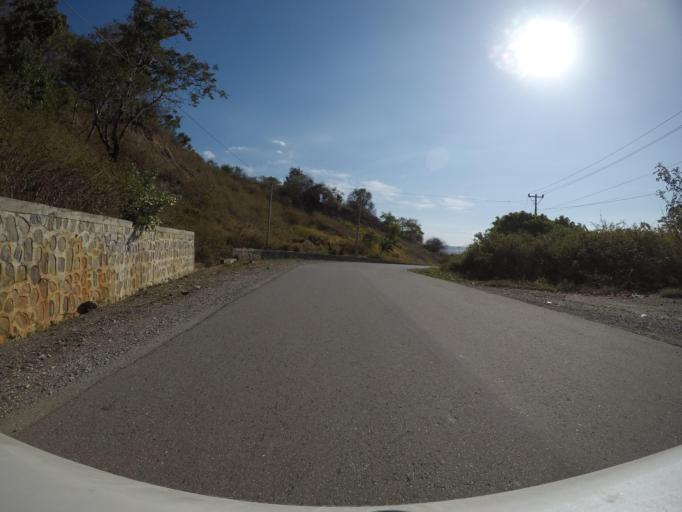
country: TL
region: Liquica
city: Maubara
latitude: -8.6352
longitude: 125.1434
